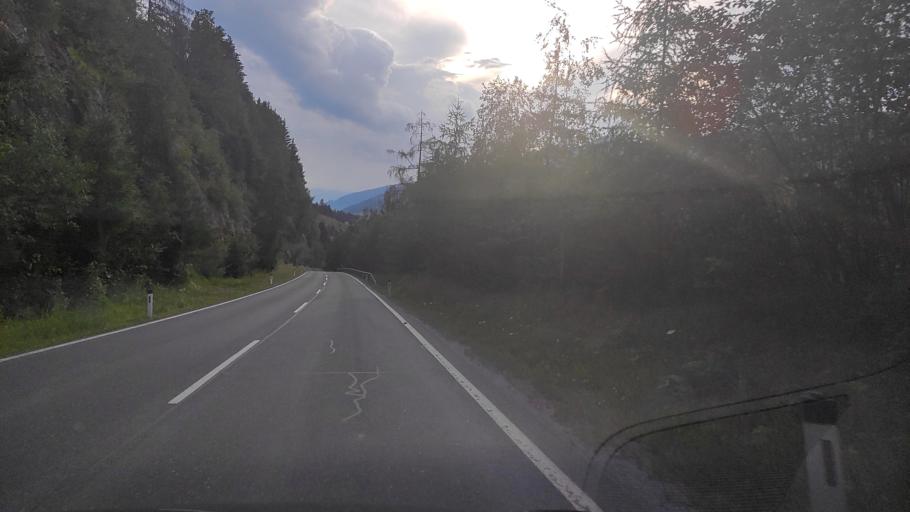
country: AT
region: Salzburg
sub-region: Politischer Bezirk Zell am See
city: Taxenbach
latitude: 47.2851
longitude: 12.9649
